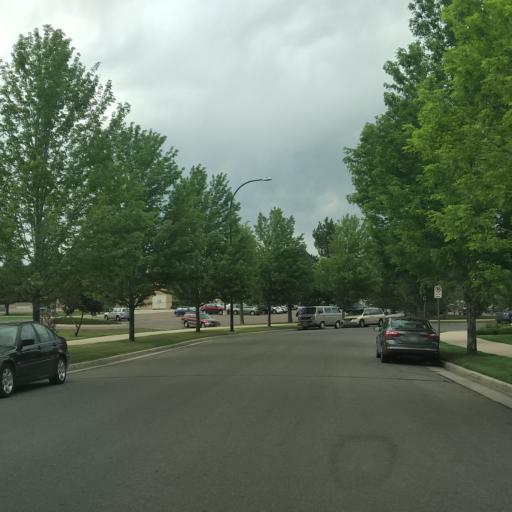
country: US
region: Colorado
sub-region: Jefferson County
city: Lakewood
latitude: 39.7050
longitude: -105.0837
